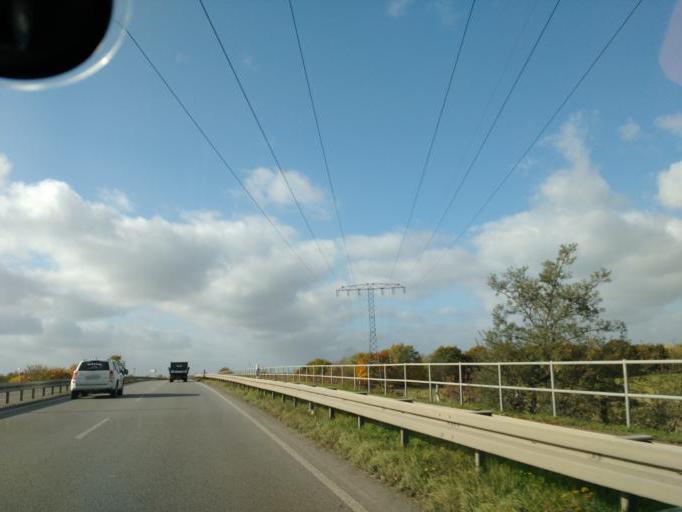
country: DE
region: Brandenburg
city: Petershagen
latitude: 52.4942
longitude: 13.7766
